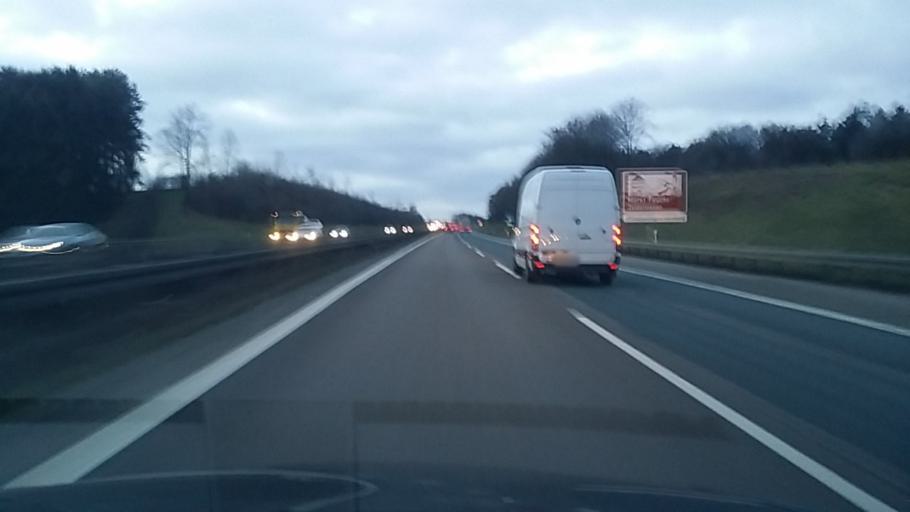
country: DE
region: Bavaria
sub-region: Regierungsbezirk Mittelfranken
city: Altdorf
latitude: 49.3712
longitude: 11.3909
